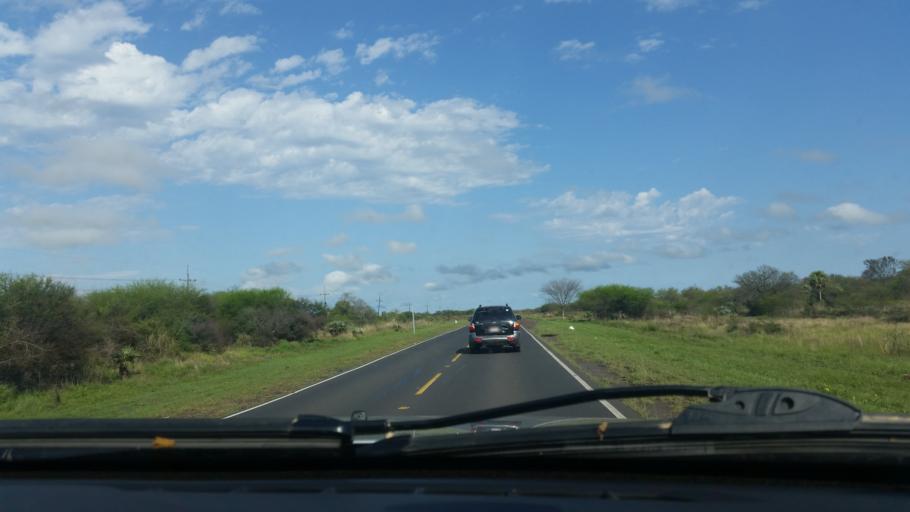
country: PY
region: Presidente Hayes
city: Benjamin Aceval
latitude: -24.9220
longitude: -57.5796
